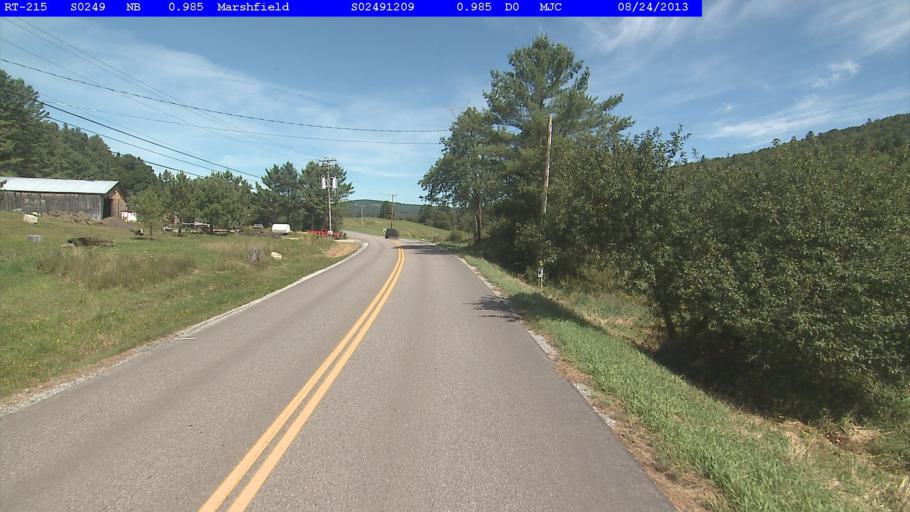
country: US
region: Vermont
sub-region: Caledonia County
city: Hardwick
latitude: 44.3618
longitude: -72.3365
